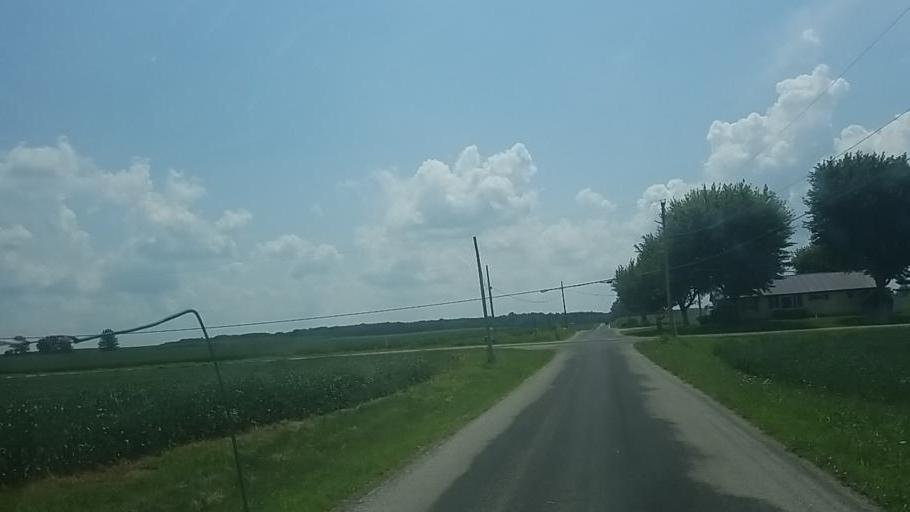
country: US
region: Ohio
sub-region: Marion County
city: Marion
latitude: 40.6885
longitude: -83.1686
